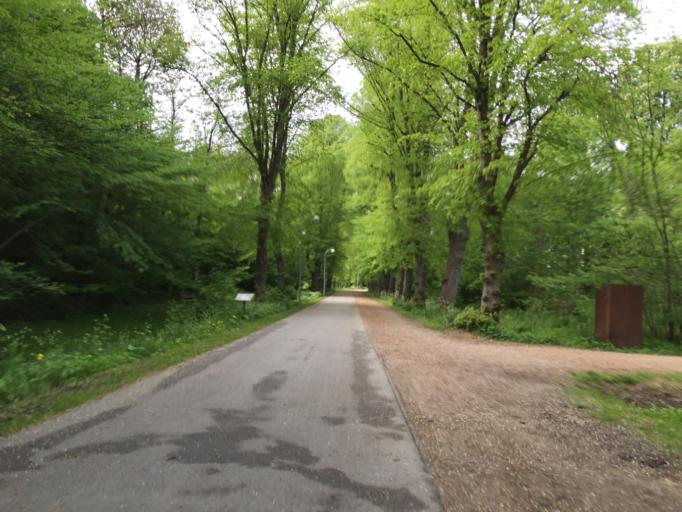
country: DK
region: Capital Region
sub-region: Brondby Kommune
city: Brondbyvester
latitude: 55.6242
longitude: 12.4445
